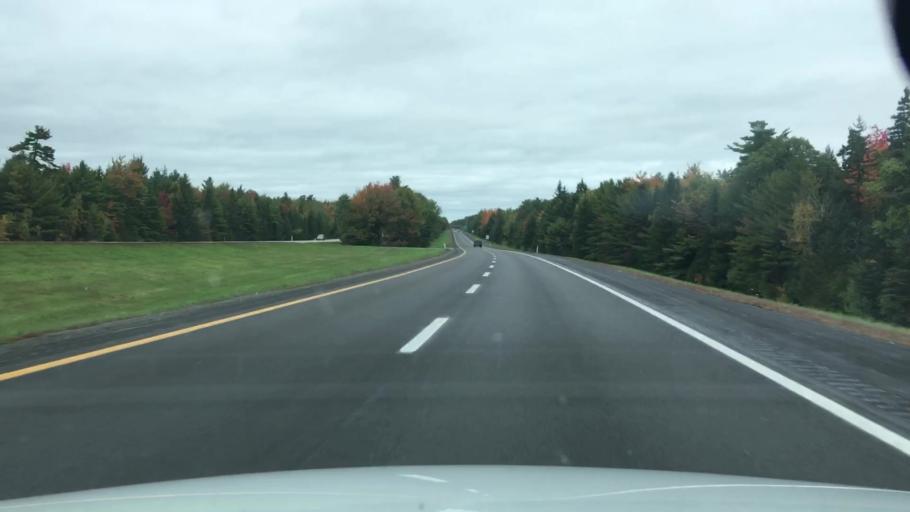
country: US
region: Maine
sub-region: Penobscot County
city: Orono
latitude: 44.8783
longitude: -68.6981
